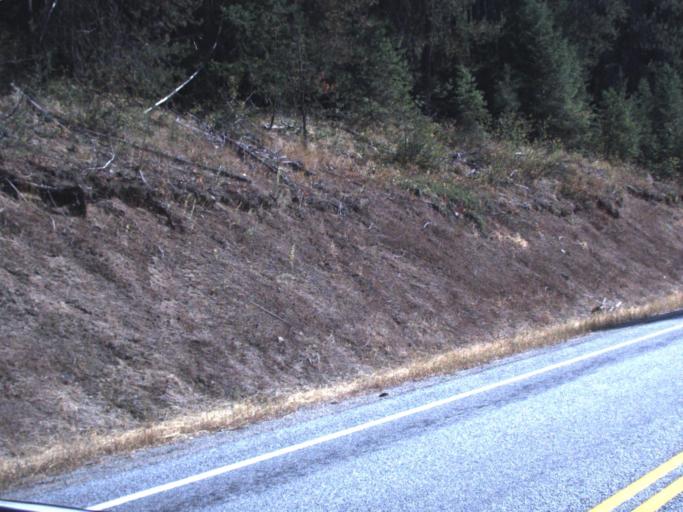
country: US
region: Washington
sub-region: Pend Oreille County
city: Newport
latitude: 48.1191
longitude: -117.2733
